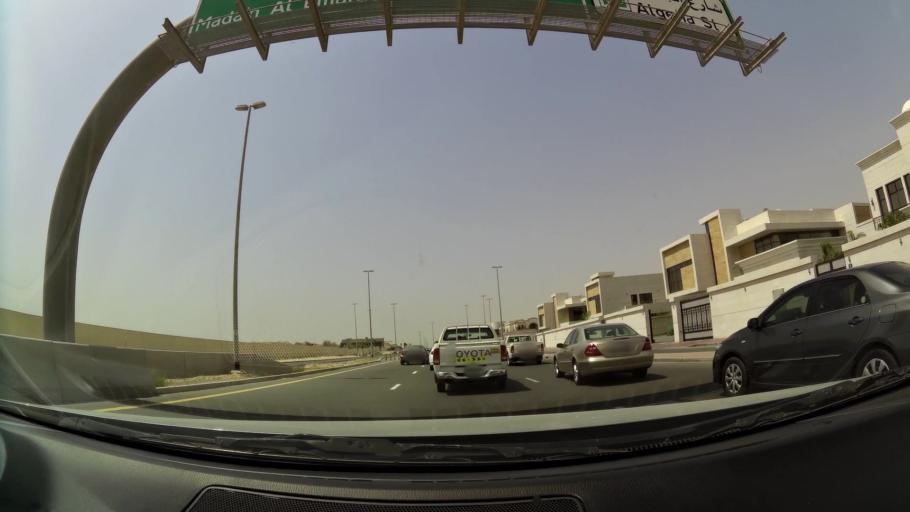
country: AE
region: Ash Shariqah
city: Sharjah
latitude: 25.2378
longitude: 55.4195
